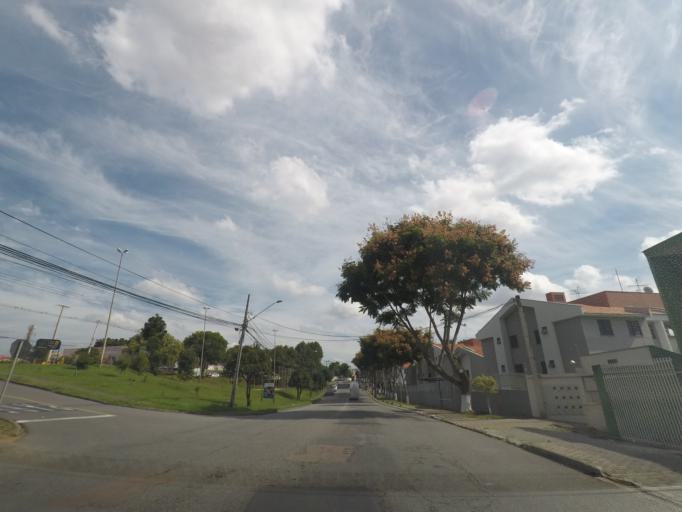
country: BR
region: Parana
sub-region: Sao Jose Dos Pinhais
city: Sao Jose dos Pinhais
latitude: -25.4939
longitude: -49.2630
